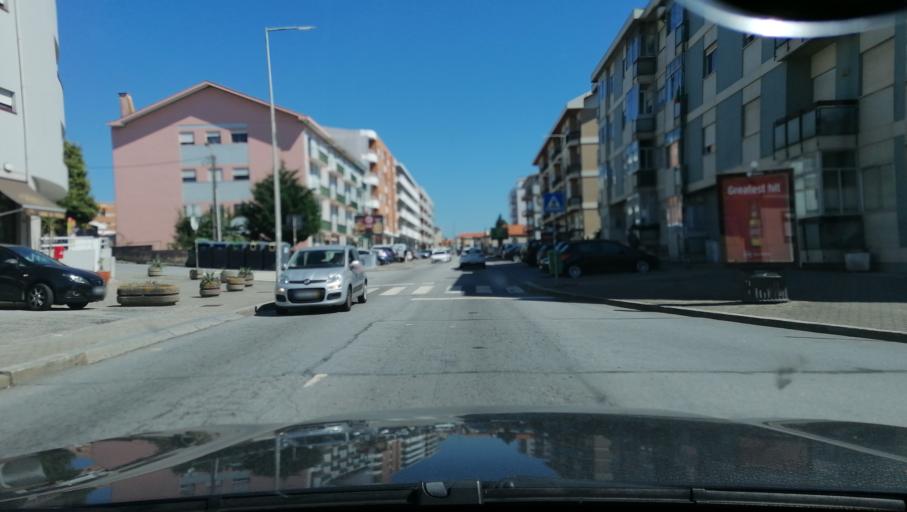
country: PT
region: Porto
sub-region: Vila Nova de Gaia
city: Canidelo
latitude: 41.1293
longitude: -8.6436
